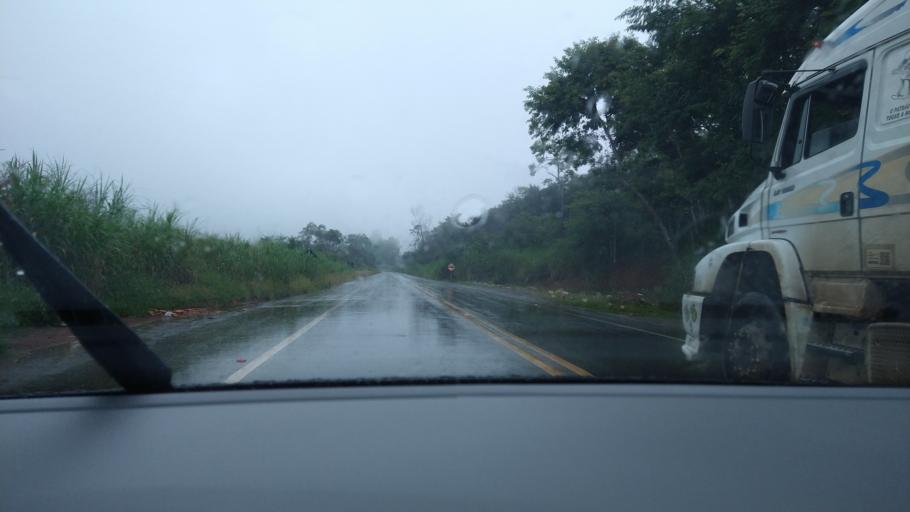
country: BR
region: Minas Gerais
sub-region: Ponte Nova
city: Ponte Nova
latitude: -20.5703
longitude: -42.8722
